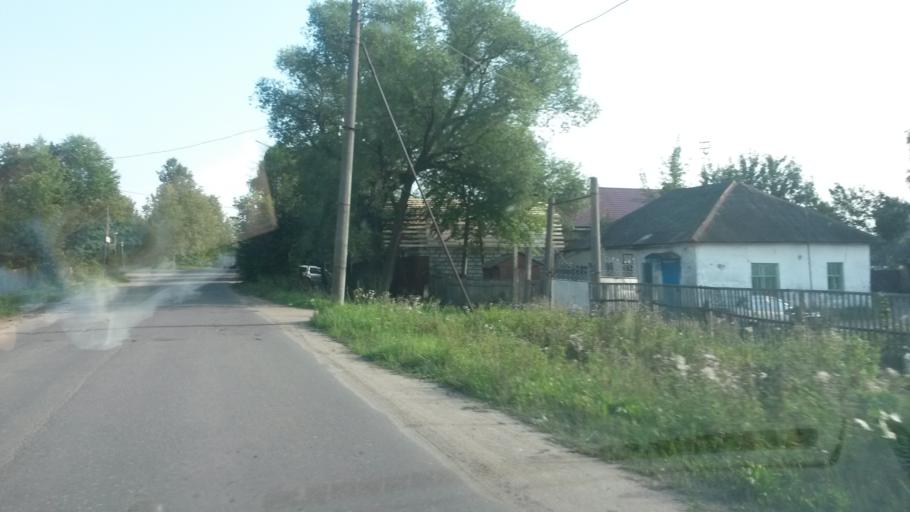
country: RU
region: Jaroslavl
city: Petrovsk
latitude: 57.0069
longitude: 39.2713
